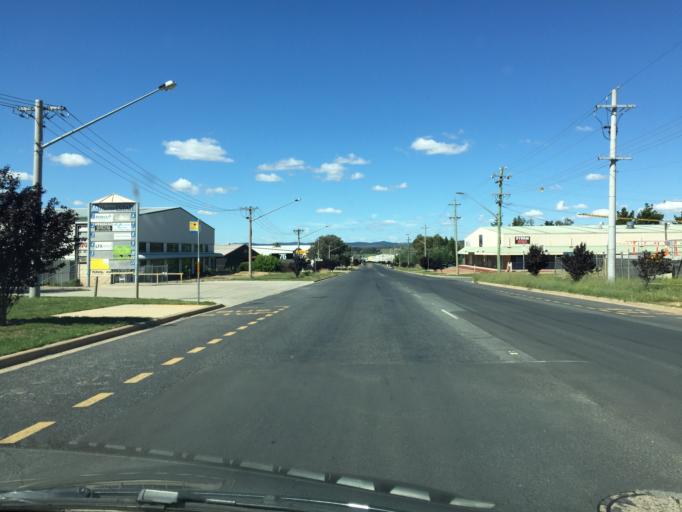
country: AU
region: Australian Capital Territory
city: Macarthur
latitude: -35.3930
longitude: 149.1643
